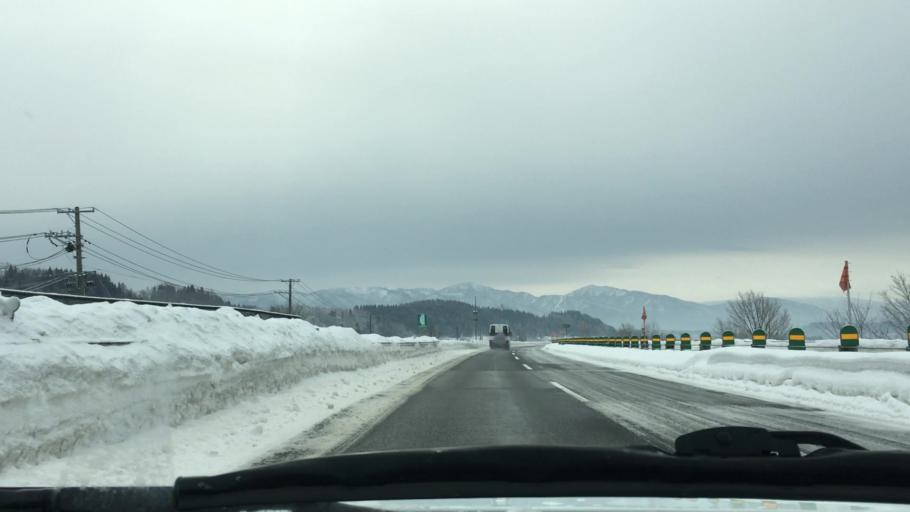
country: JP
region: Akita
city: Hanawa
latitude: 40.2938
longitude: 140.7560
